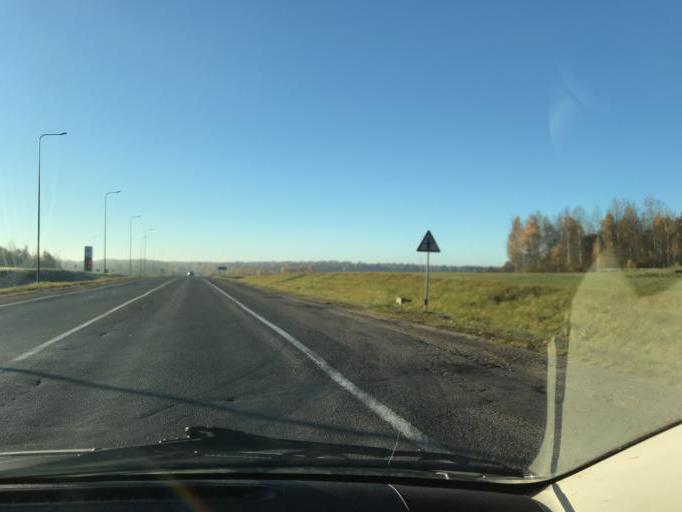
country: BY
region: Vitebsk
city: Vitebsk
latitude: 54.9112
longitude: 30.3758
